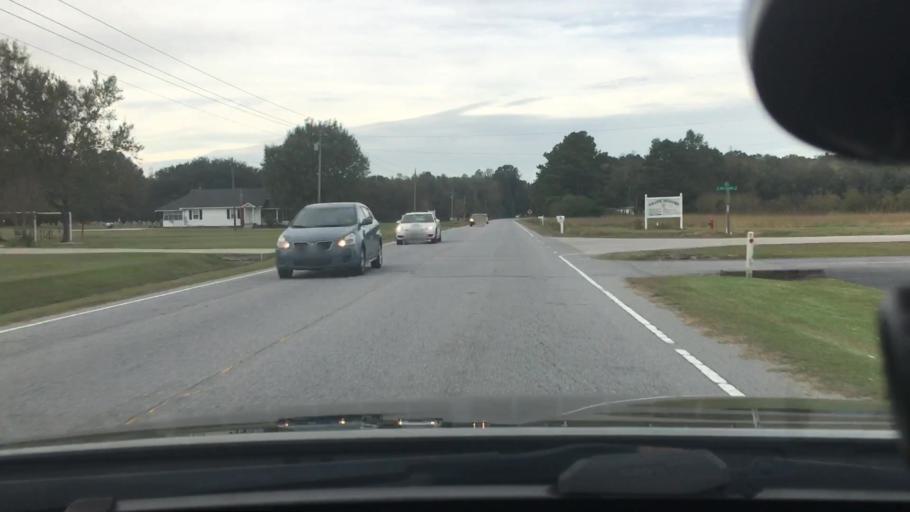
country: US
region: North Carolina
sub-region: Pitt County
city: Windsor
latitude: 35.4314
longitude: -77.2622
